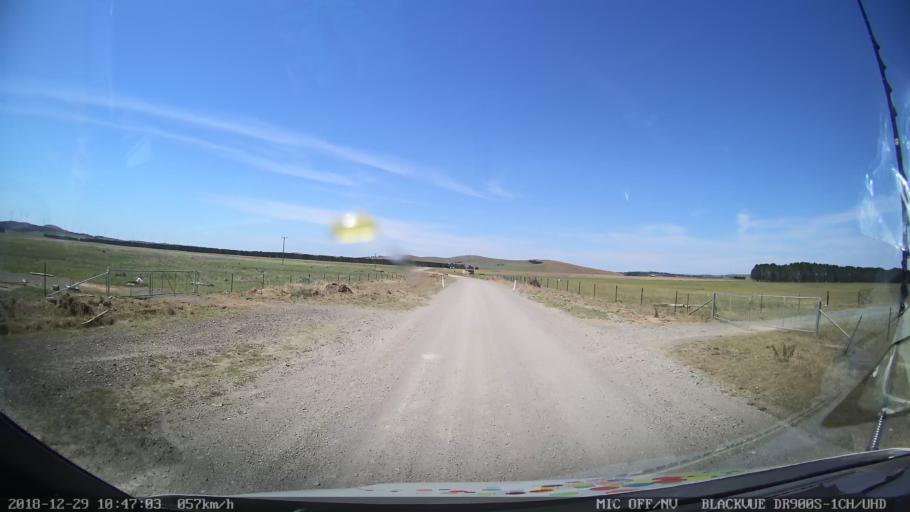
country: AU
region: New South Wales
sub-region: Palerang
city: Bungendore
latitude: -35.0560
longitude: 149.5158
